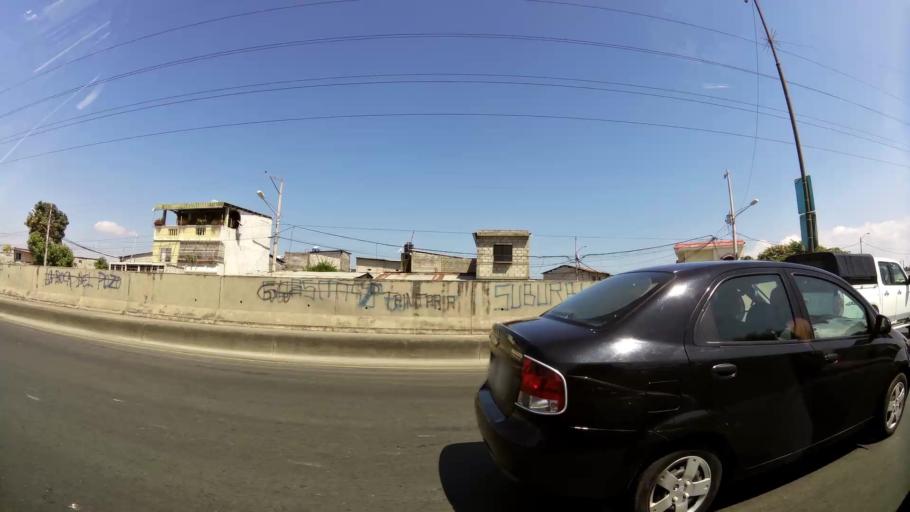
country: EC
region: Guayas
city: Guayaquil
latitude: -2.2327
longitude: -79.9447
